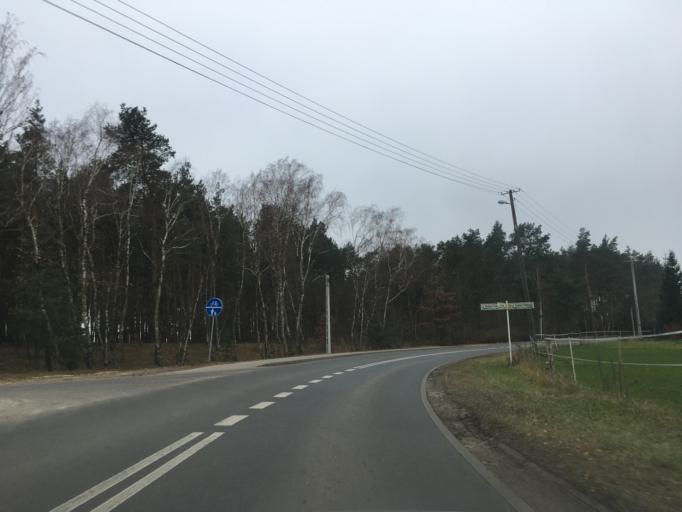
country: PL
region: Masovian Voivodeship
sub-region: Powiat piaseczynski
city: Lesznowola
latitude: 52.0670
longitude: 20.9336
